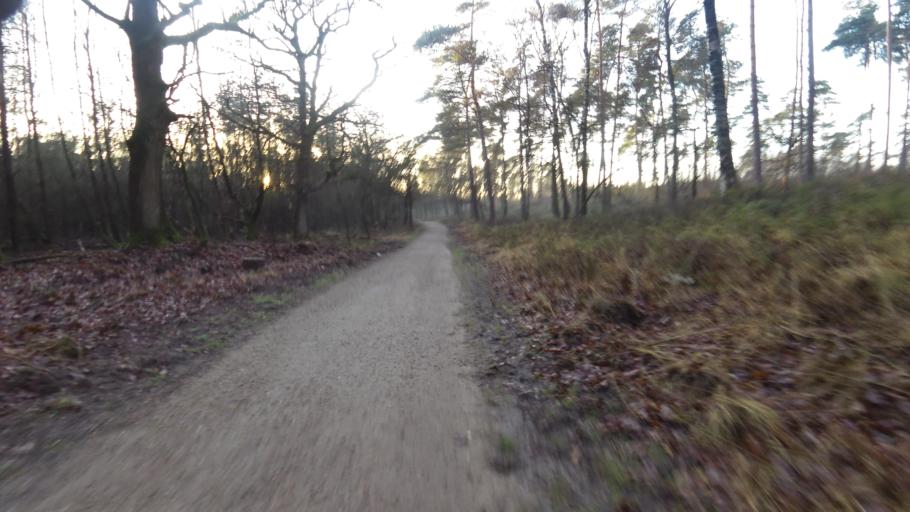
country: NL
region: Gelderland
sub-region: Gemeente Apeldoorn
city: Uddel
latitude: 52.2290
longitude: 5.8440
